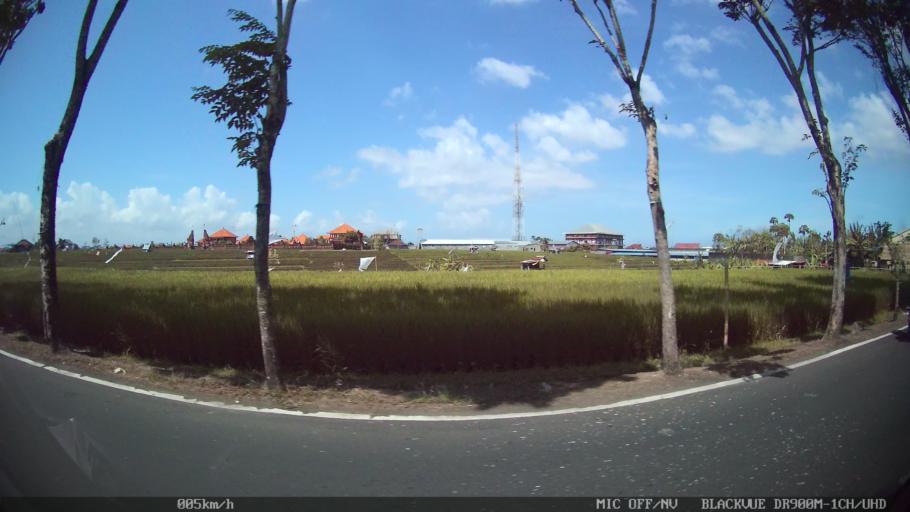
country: ID
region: Bali
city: Banjar Kertasari
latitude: -8.6260
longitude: 115.1821
